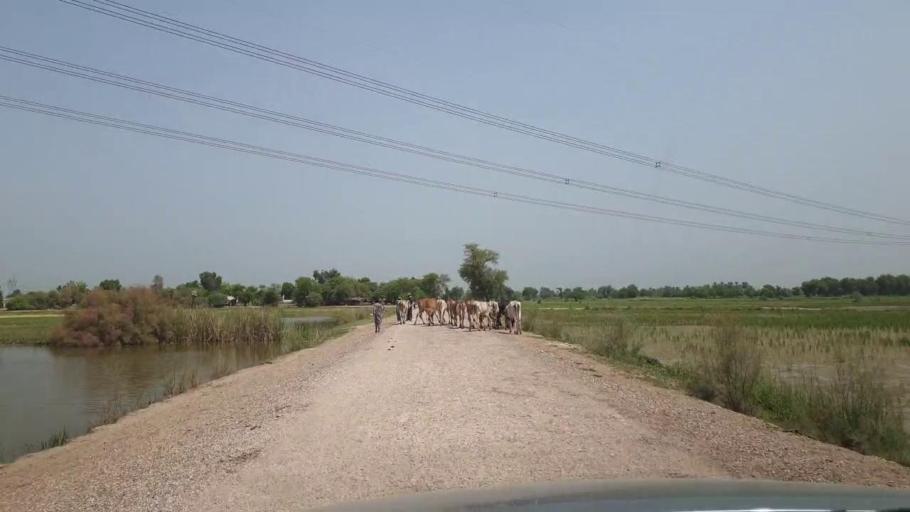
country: PK
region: Sindh
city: Madeji
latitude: 27.8058
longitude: 68.5203
